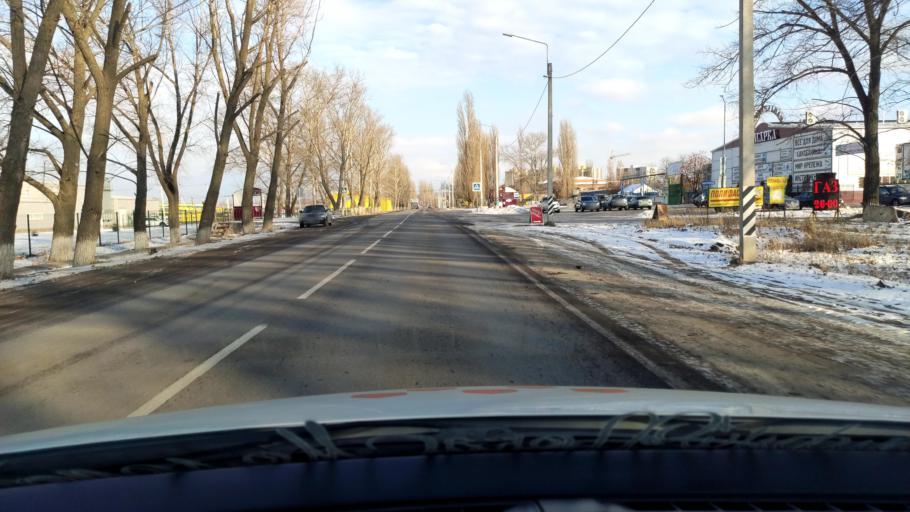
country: RU
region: Voronezj
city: Semiluki
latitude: 51.6904
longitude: 38.9931
